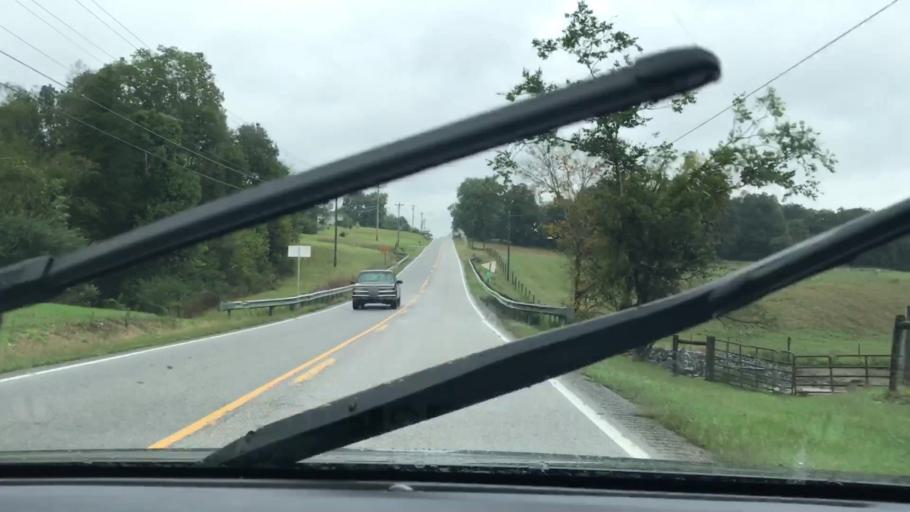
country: US
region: Kentucky
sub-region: Monroe County
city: Tompkinsville
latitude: 36.6772
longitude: -85.7180
